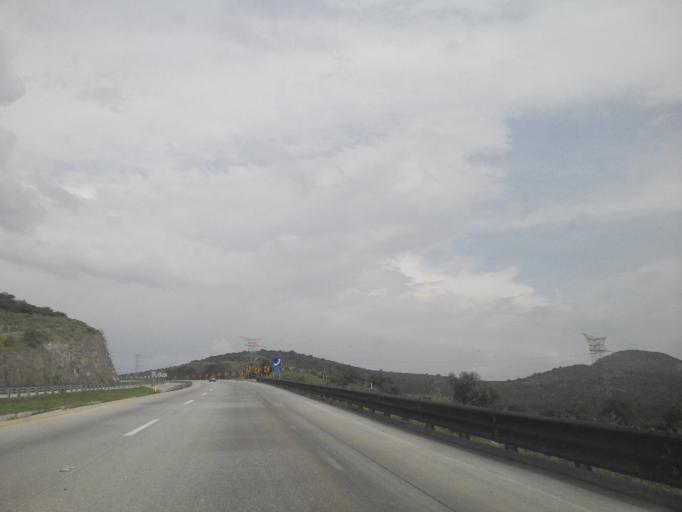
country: MX
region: Mexico
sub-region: Apaxco
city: Colonia Juarez
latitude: 20.0232
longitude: -99.1687
